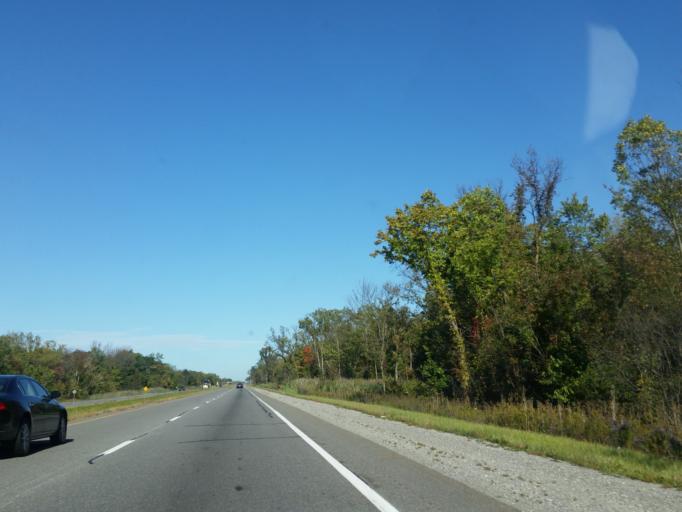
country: US
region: New York
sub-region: Niagara County
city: Niagara Falls
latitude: 43.0085
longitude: -79.0805
